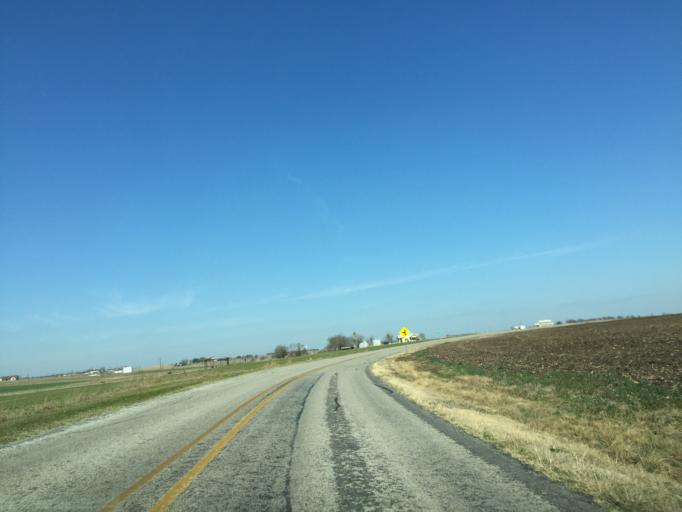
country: US
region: Texas
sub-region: Williamson County
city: Serenada
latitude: 30.7013
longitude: -97.5896
